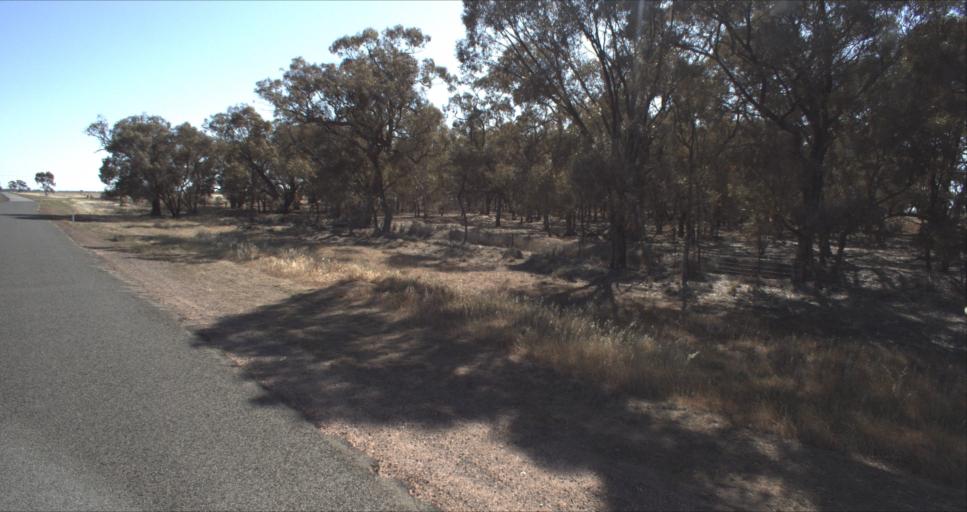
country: AU
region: New South Wales
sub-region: Leeton
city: Leeton
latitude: -34.5636
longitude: 146.2648
